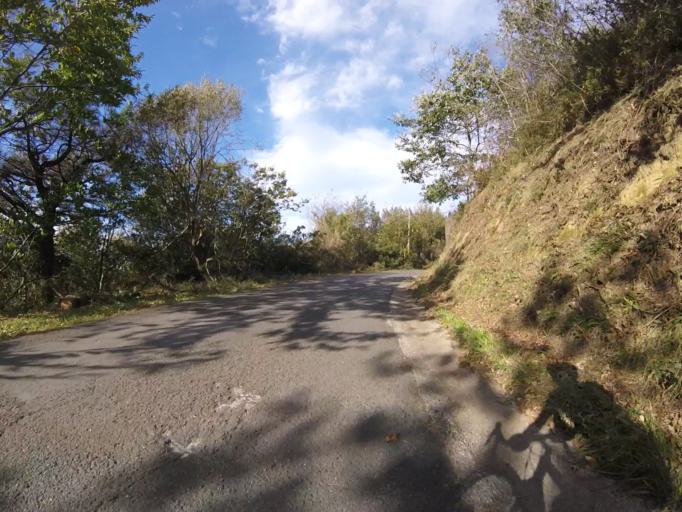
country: ES
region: Basque Country
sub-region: Provincia de Guipuzcoa
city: Orio
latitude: 43.2889
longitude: -2.0996
